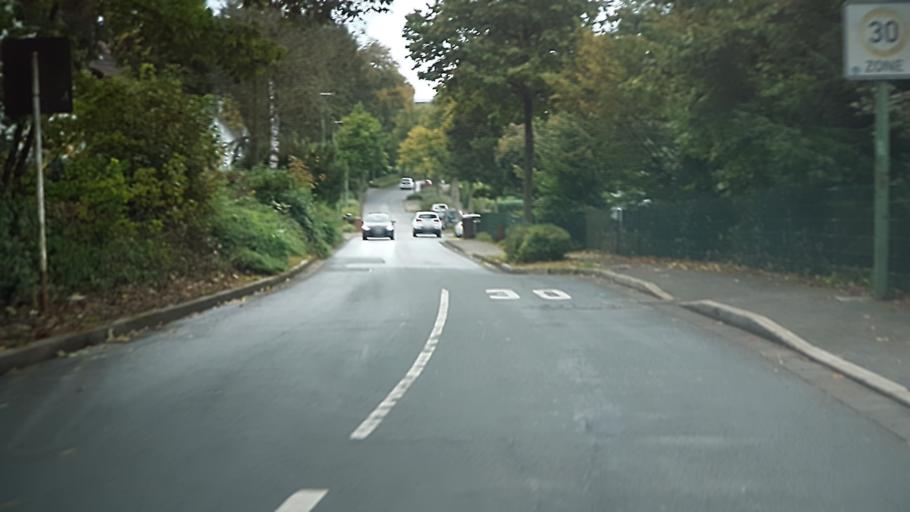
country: DE
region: North Rhine-Westphalia
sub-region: Regierungsbezirk Arnsberg
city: Luedenscheid
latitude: 51.2132
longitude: 7.6662
